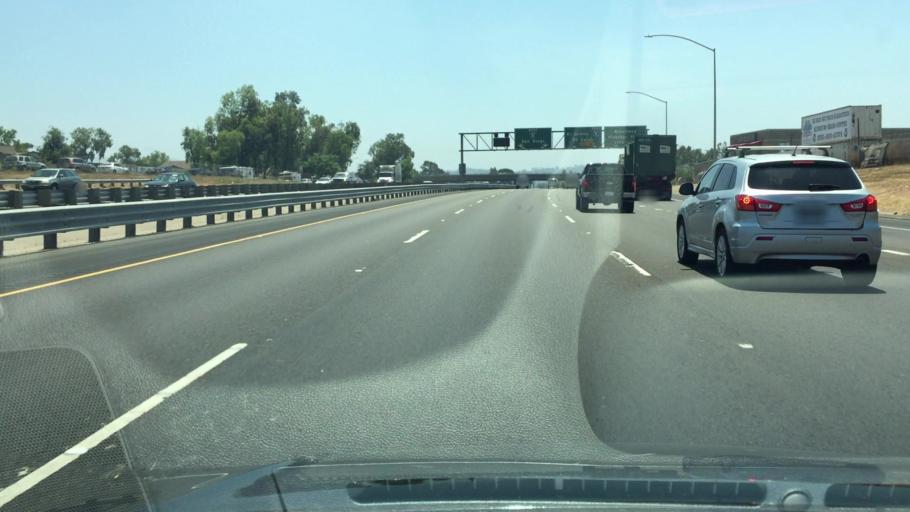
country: US
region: California
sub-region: San Diego County
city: El Cajon
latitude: 32.8169
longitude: -116.9609
